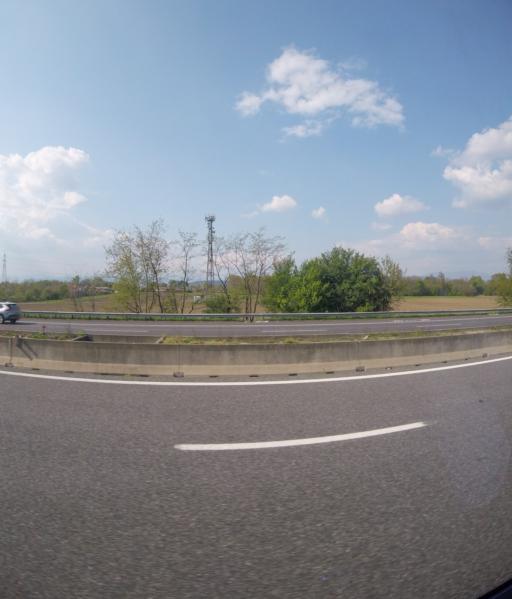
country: IT
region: Piedmont
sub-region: Provincia di Novara
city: Castelletto Sopra Ticino
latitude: 45.6988
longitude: 8.6355
